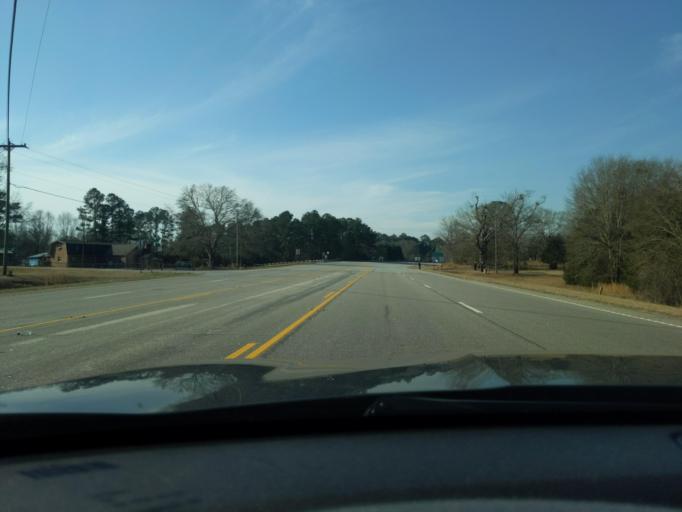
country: US
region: South Carolina
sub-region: Abbeville County
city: Abbeville
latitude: 34.1362
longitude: -82.4131
